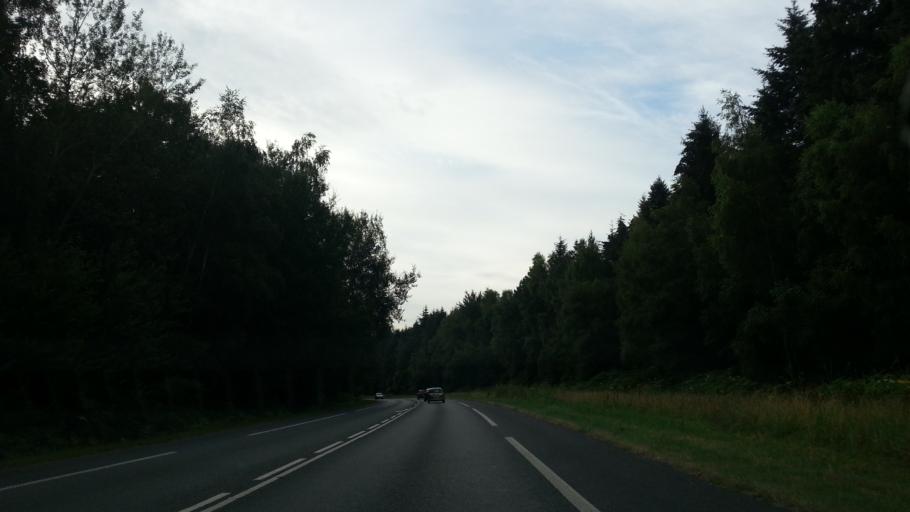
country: FR
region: Picardie
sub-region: Departement de l'Oise
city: Creil
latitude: 49.2433
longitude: 2.4956
